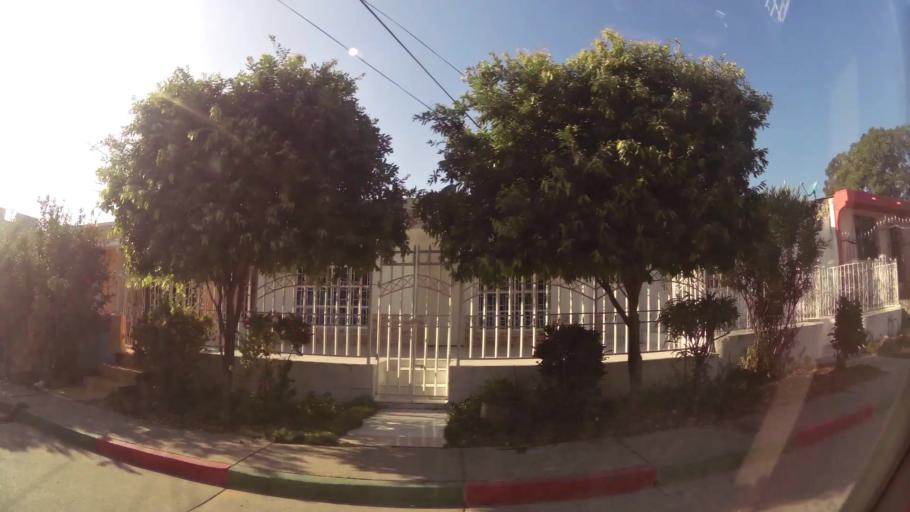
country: CO
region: Bolivar
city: Cartagena
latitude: 10.4015
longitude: -75.5016
